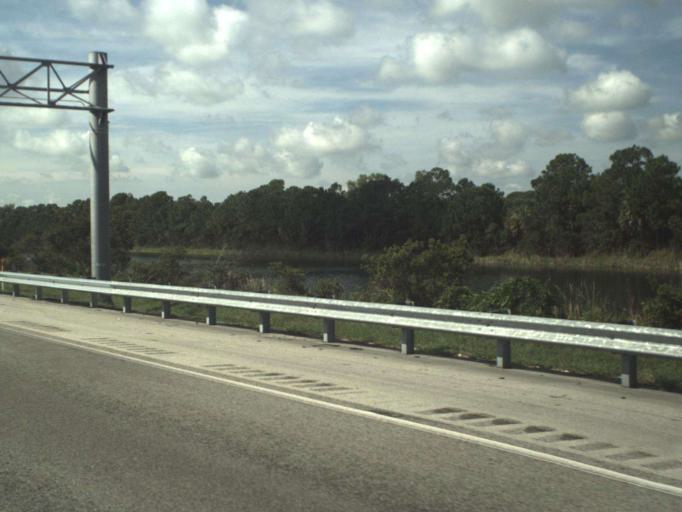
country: US
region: Florida
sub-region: Palm Beach County
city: Limestone Creek
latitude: 26.8892
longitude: -80.1323
